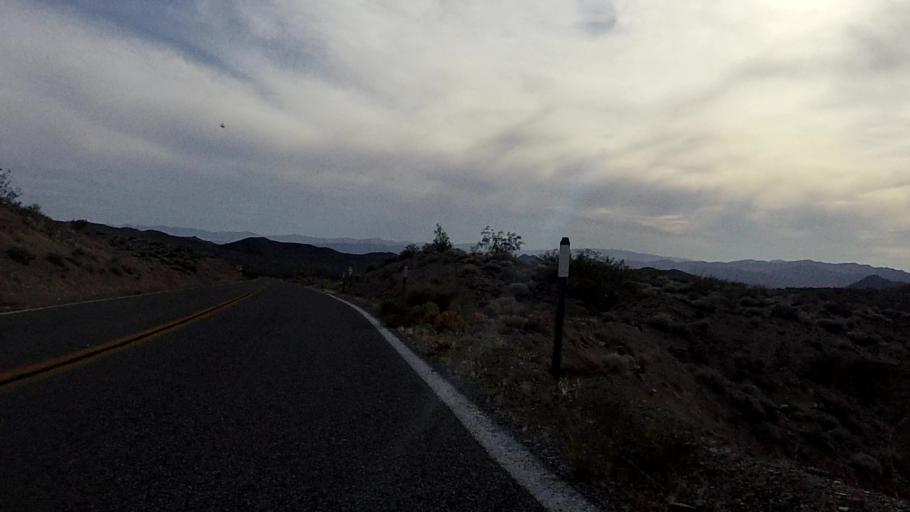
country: US
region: Nevada
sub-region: Nye County
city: Pahrump
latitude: 35.9218
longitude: -116.4343
